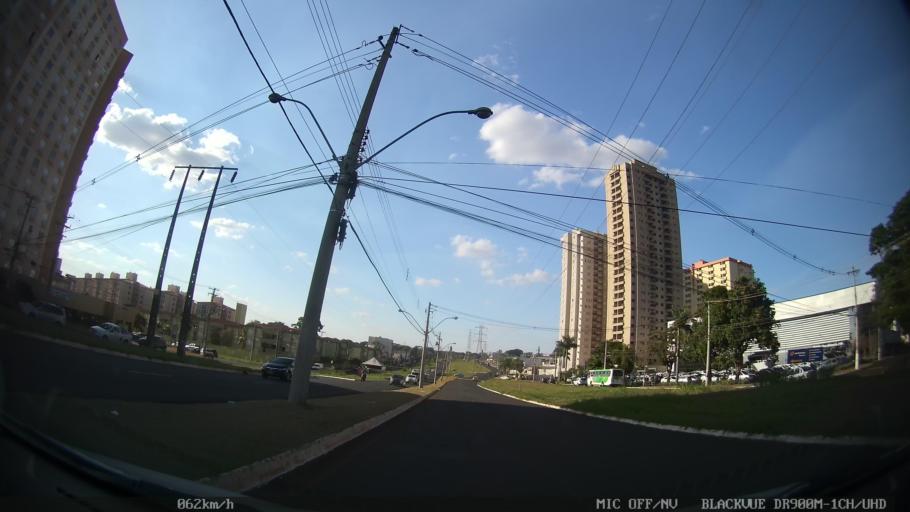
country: BR
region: Sao Paulo
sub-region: Ribeirao Preto
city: Ribeirao Preto
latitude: -21.1989
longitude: -47.7797
